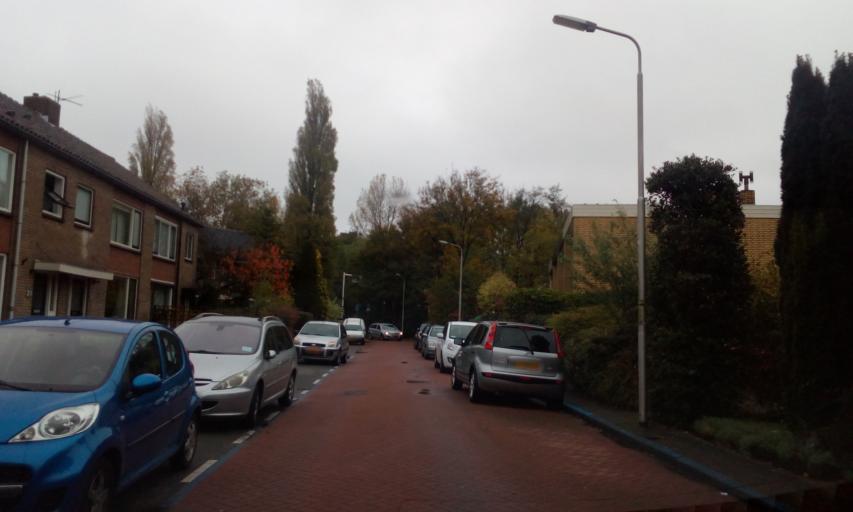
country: NL
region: South Holland
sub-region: Gemeente Lansingerland
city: Berkel en Rodenrijs
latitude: 51.9751
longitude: 4.4583
